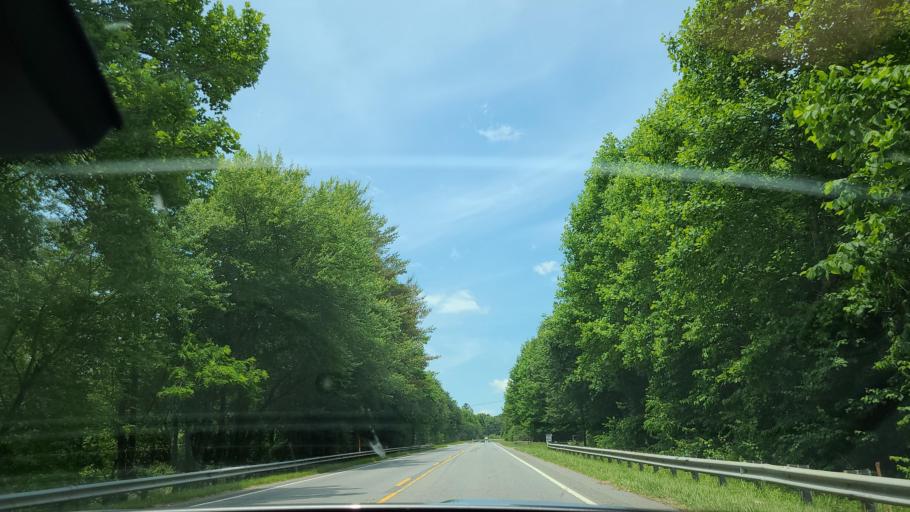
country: US
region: Georgia
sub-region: Towns County
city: Hiawassee
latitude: 35.0268
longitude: -83.7125
